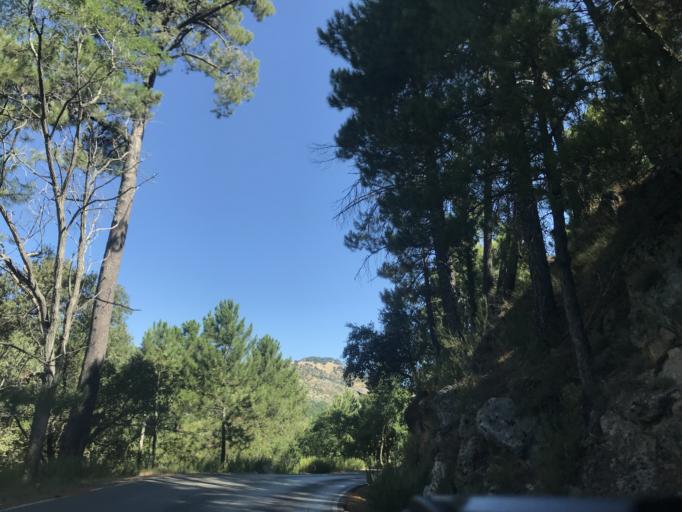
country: ES
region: Andalusia
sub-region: Provincia de Jaen
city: La Iruela
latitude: 37.9193
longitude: -2.9458
